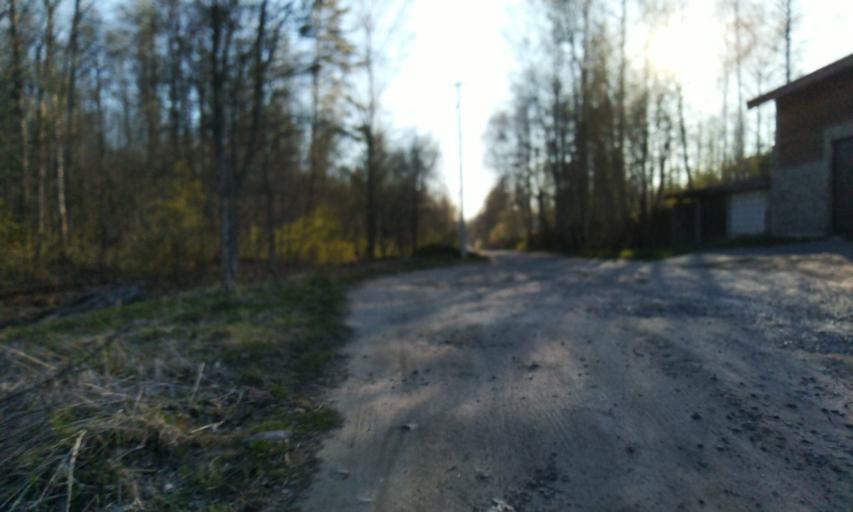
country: RU
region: Leningrad
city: Toksovo
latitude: 60.1400
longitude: 30.5635
